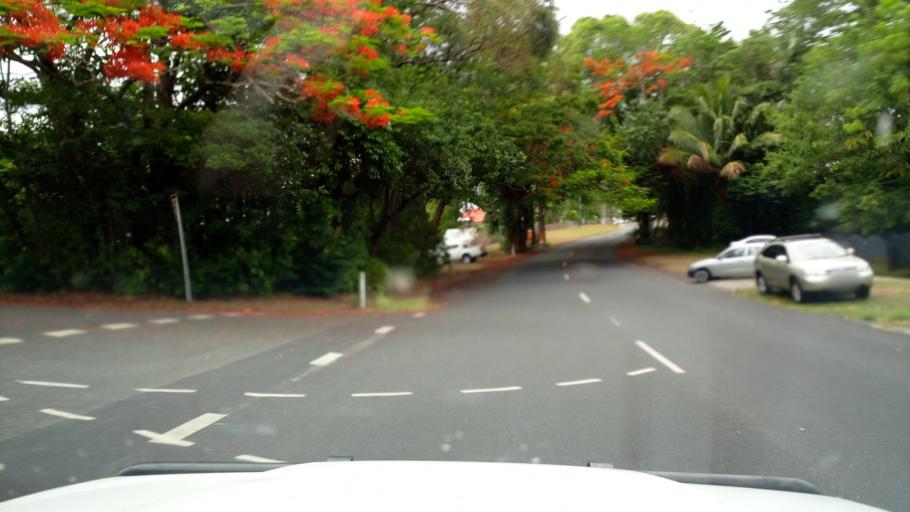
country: AU
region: Queensland
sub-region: Cairns
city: Redlynch
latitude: -16.8832
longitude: 145.7134
